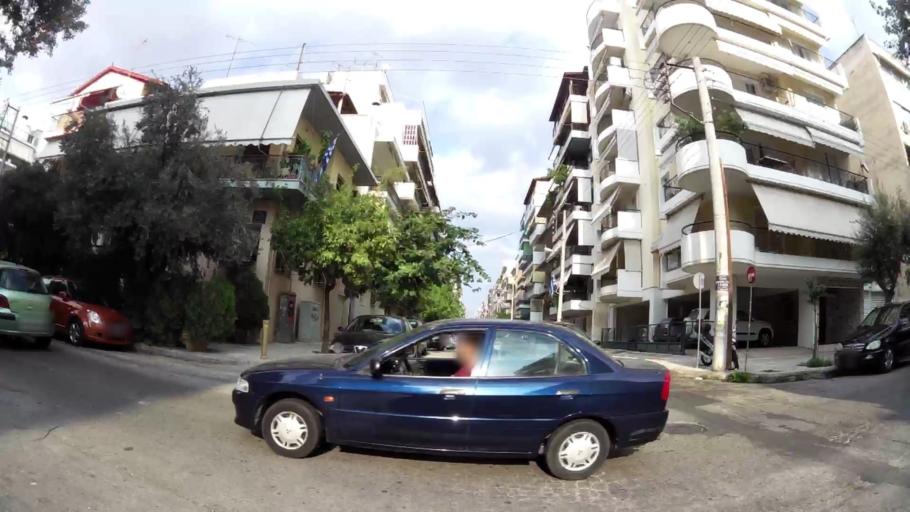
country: GR
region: Attica
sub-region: Nomarchia Athinas
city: Kallithea
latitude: 37.9488
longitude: 23.7012
